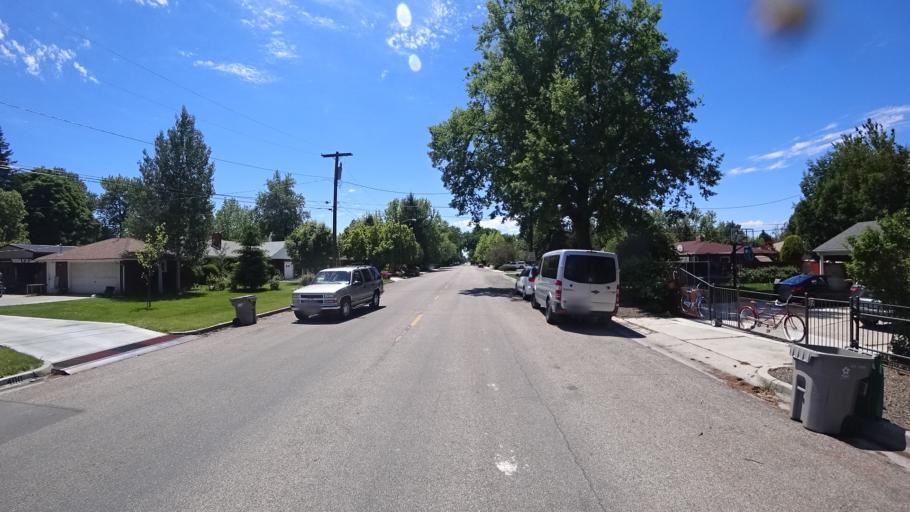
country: US
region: Idaho
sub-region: Ada County
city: Boise
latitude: 43.6004
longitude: -116.2236
